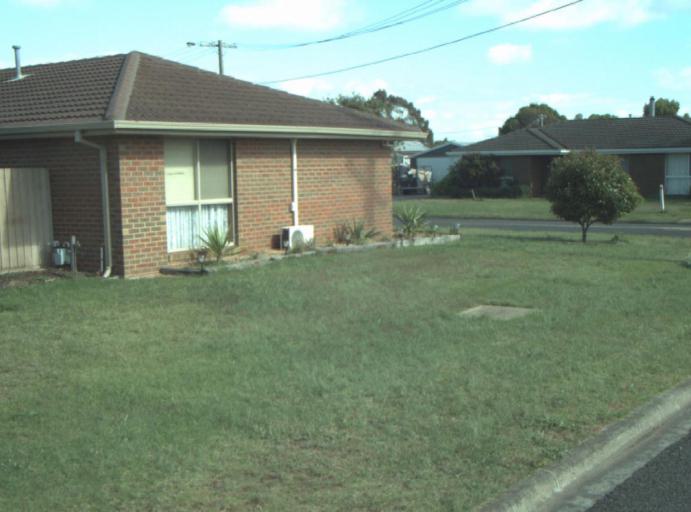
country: AU
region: Victoria
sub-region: Greater Geelong
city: Lara
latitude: -38.0172
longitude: 144.3860
